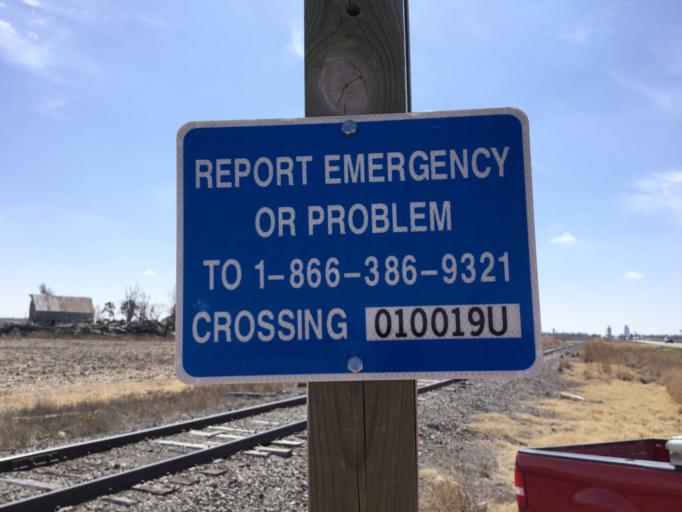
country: US
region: Kansas
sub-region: Pawnee County
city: Larned
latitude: 38.2757
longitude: -98.9570
